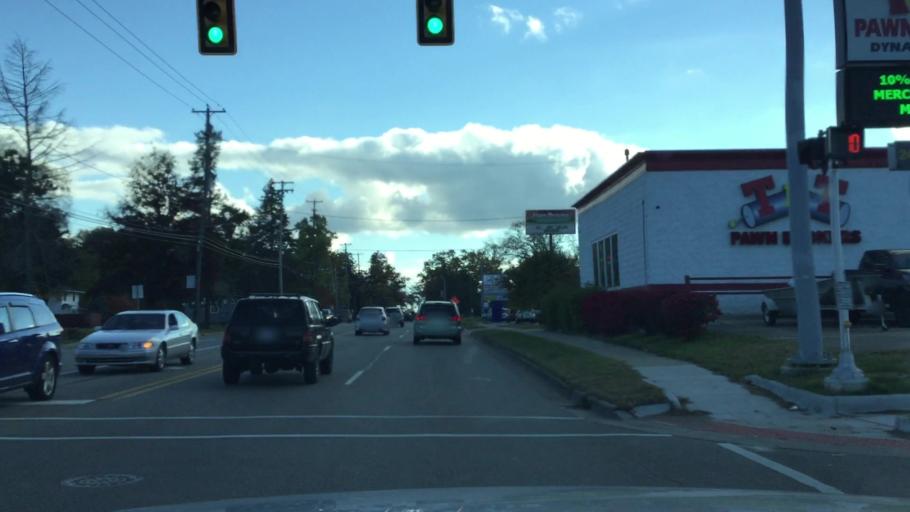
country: US
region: Michigan
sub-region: Kalamazoo County
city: Kalamazoo
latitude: 42.2519
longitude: -85.5897
